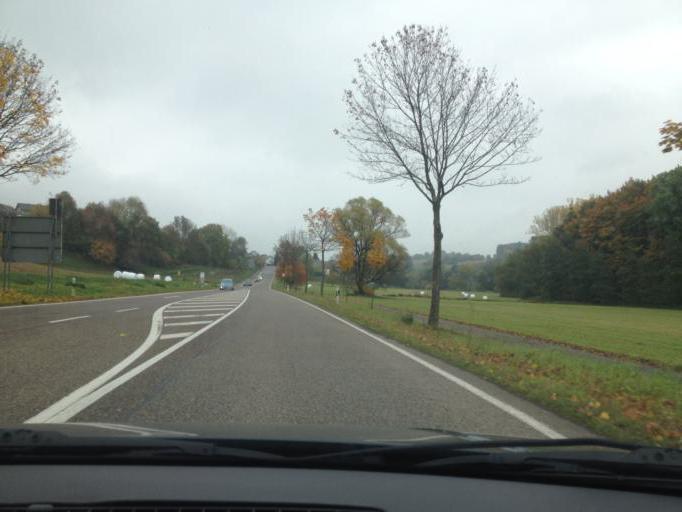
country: DE
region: Saarland
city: Tholey
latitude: 49.4593
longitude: 6.9847
